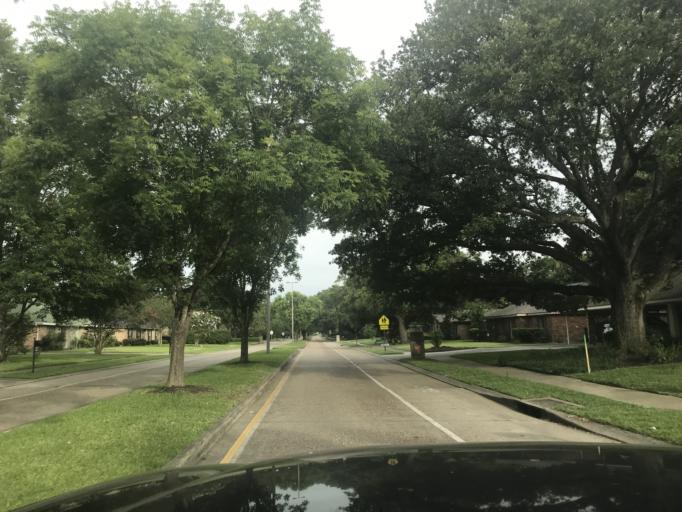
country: US
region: Louisiana
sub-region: Lafayette Parish
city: Lafayette
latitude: 30.1958
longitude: -92.0467
